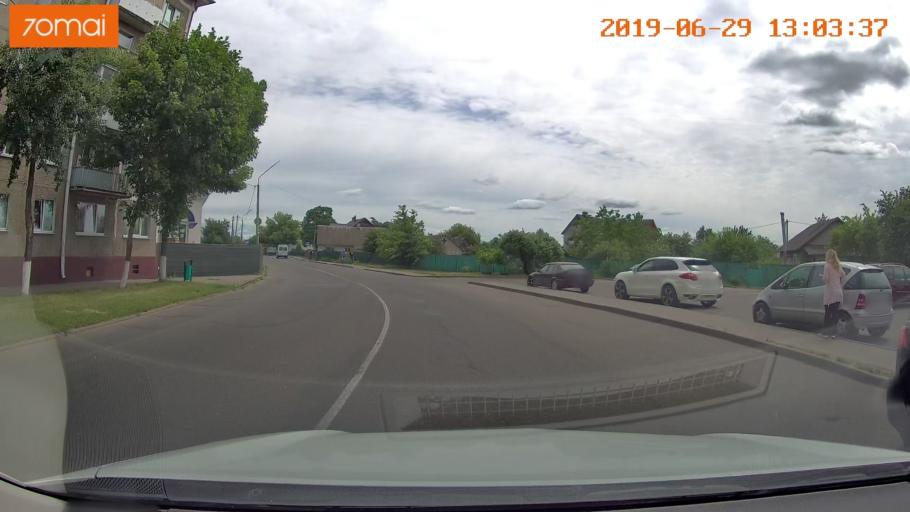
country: BY
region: Minsk
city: Slutsk
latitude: 53.0314
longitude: 27.5627
